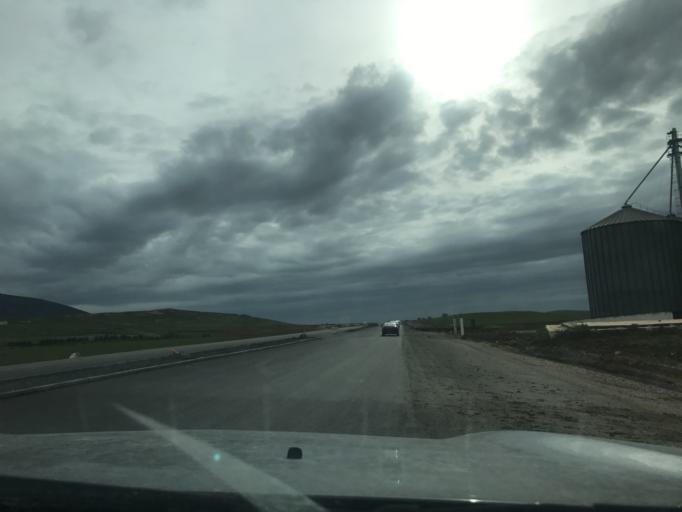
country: TN
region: Silyanah
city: Siliana
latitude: 36.1098
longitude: 9.5893
